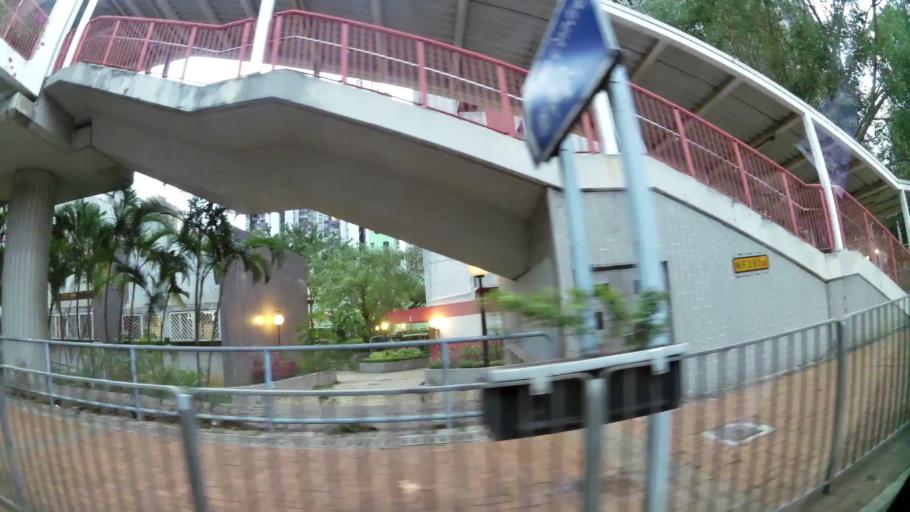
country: HK
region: Tsuen Wan
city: Tsuen Wan
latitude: 22.3562
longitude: 114.1022
